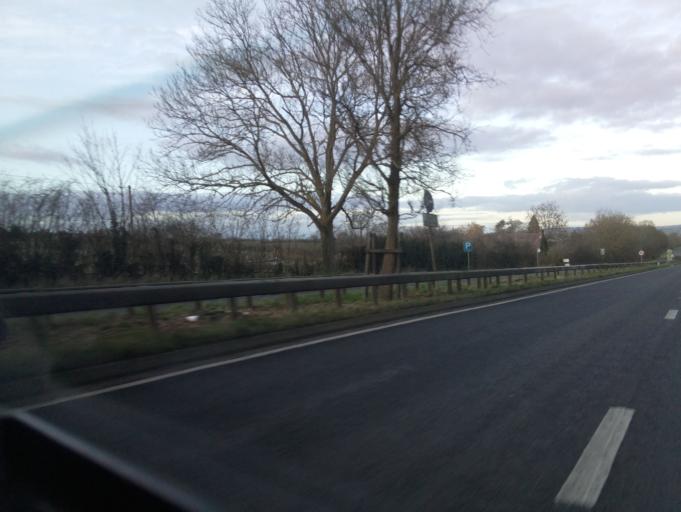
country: GB
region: England
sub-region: Staffordshire
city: Stone
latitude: 52.8615
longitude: -2.1322
